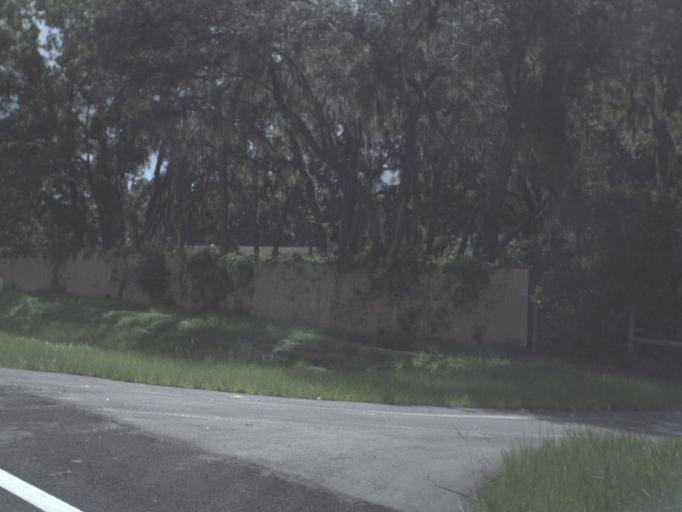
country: US
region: Florida
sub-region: Hillsborough County
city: Temple Terrace
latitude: 28.0433
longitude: -82.3474
